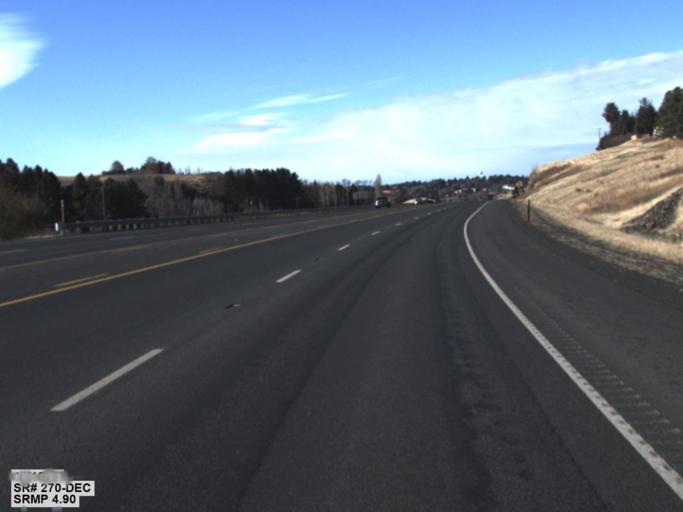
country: US
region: Washington
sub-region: Whitman County
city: Pullman
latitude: 46.7213
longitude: -117.1360
